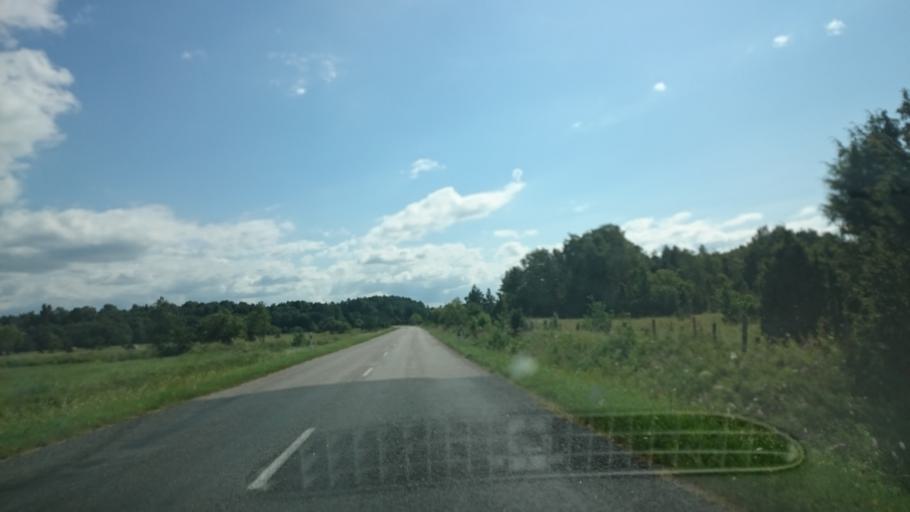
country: EE
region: Saare
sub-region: Orissaare vald
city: Orissaare
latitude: 58.5750
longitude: 22.7625
